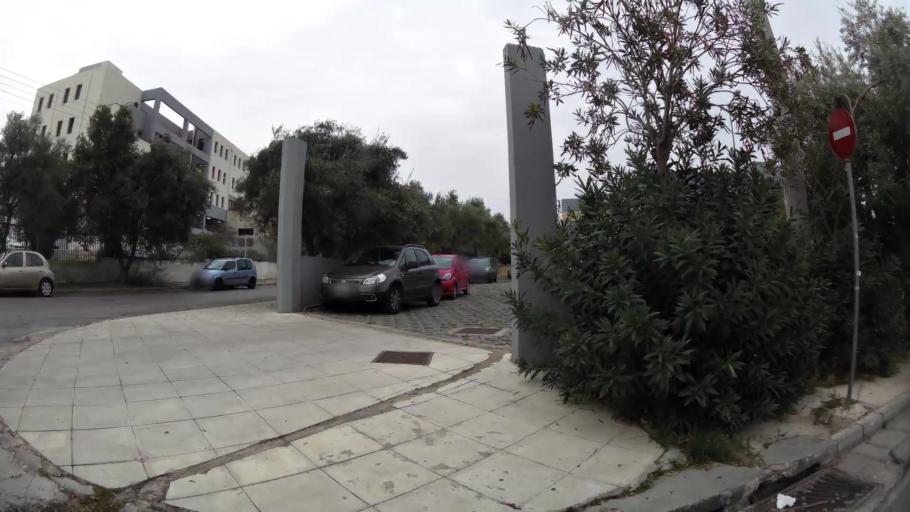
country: GR
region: Attica
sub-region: Nomarchia Athinas
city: Argyroupoli
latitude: 37.9140
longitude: 23.7424
